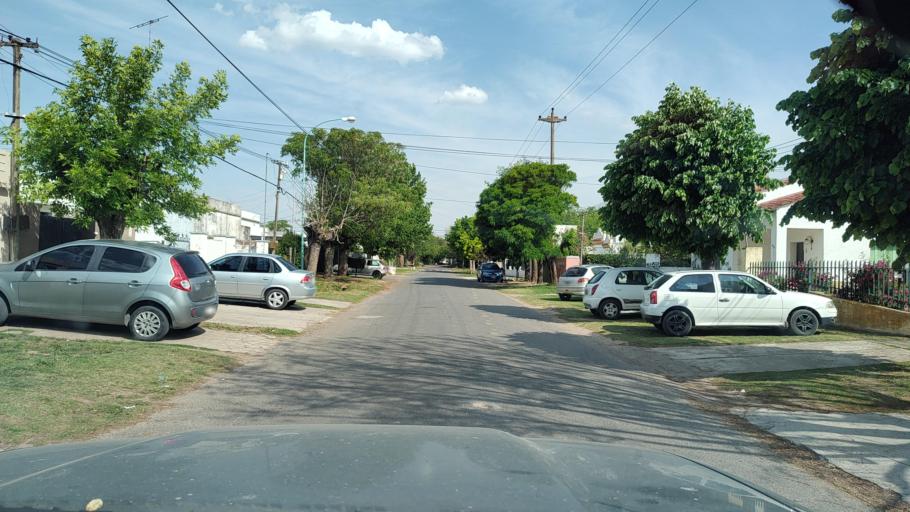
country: AR
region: Buenos Aires
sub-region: Partido de Lujan
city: Lujan
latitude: -34.5989
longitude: -59.1773
